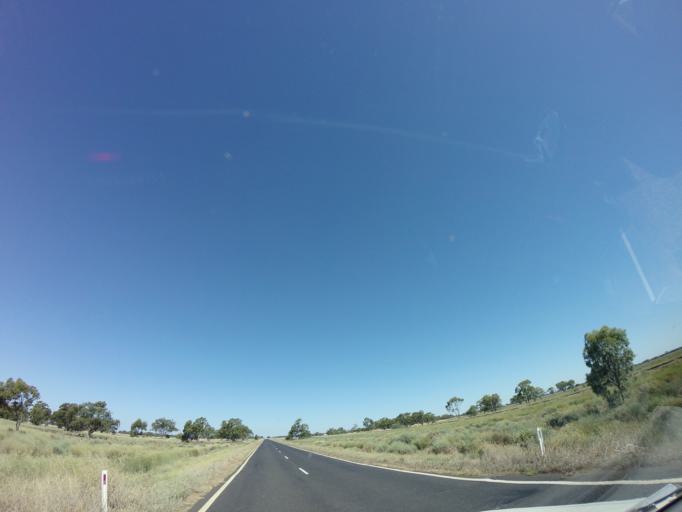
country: AU
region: New South Wales
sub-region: Bogan
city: Nyngan
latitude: -31.6828
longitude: 147.4246
